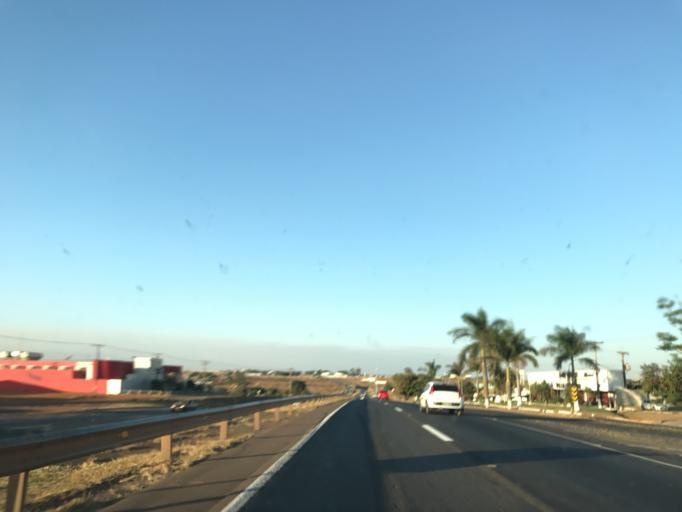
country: BR
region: Goias
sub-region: Anapolis
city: Anapolis
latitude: -16.3692
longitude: -48.9404
